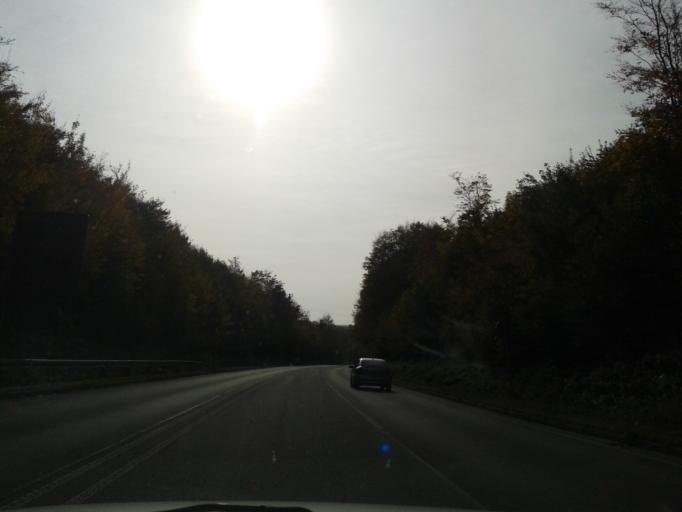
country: DE
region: North Rhine-Westphalia
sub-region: Regierungsbezirk Arnsberg
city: Ruthen
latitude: 51.5064
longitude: 8.4546
